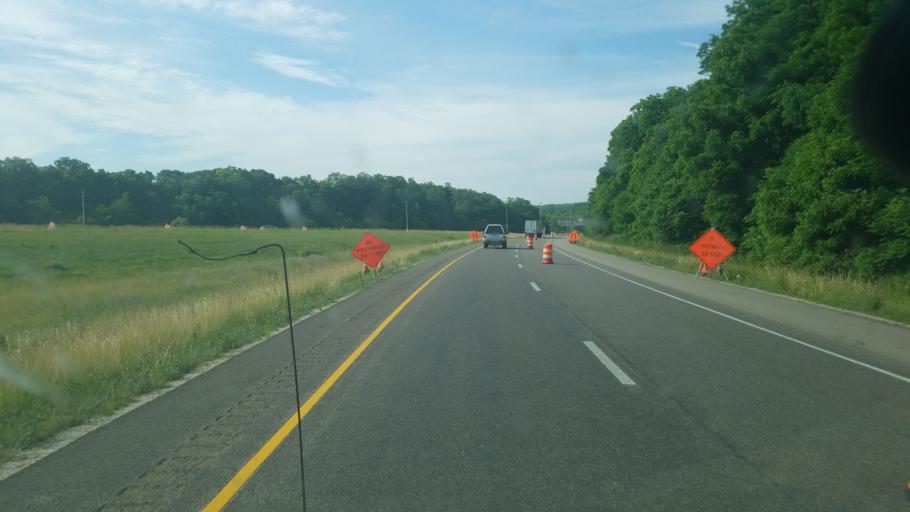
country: US
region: Illinois
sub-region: Peoria County
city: Bellevue
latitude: 40.7383
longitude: -89.6704
